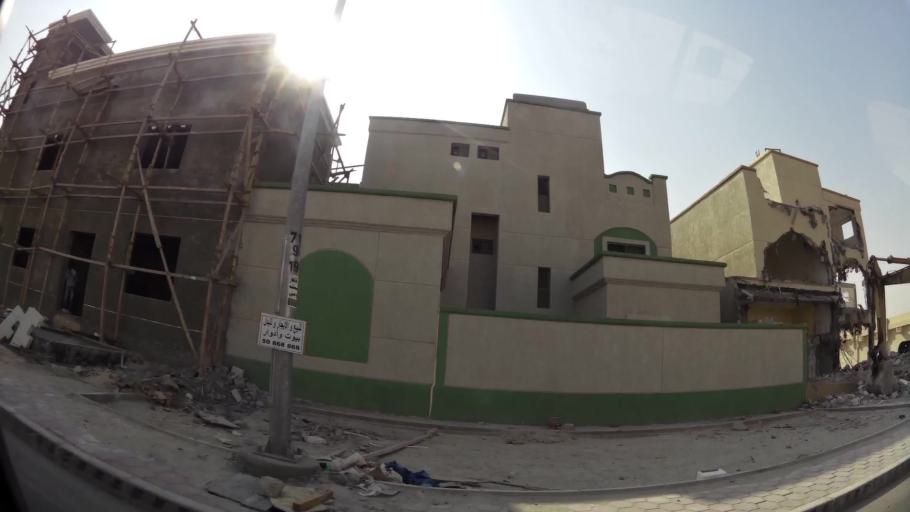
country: KW
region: Muhafazat al Jahra'
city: Al Jahra'
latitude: 29.3495
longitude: 47.7612
